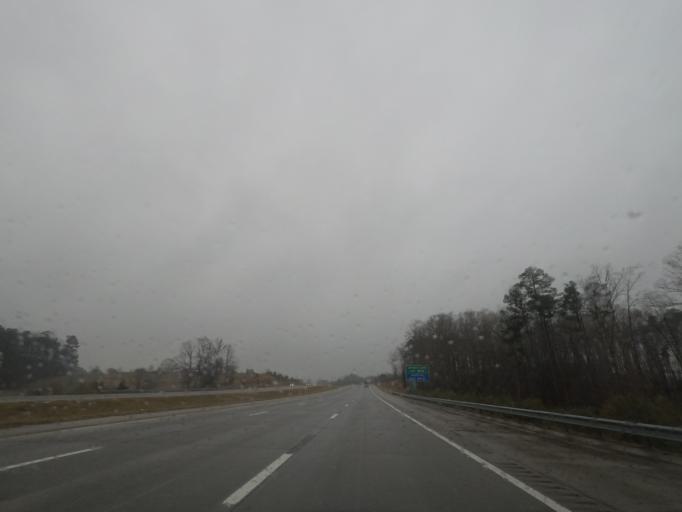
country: US
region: North Carolina
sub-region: Wake County
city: Green Level
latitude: 35.7628
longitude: -78.8896
